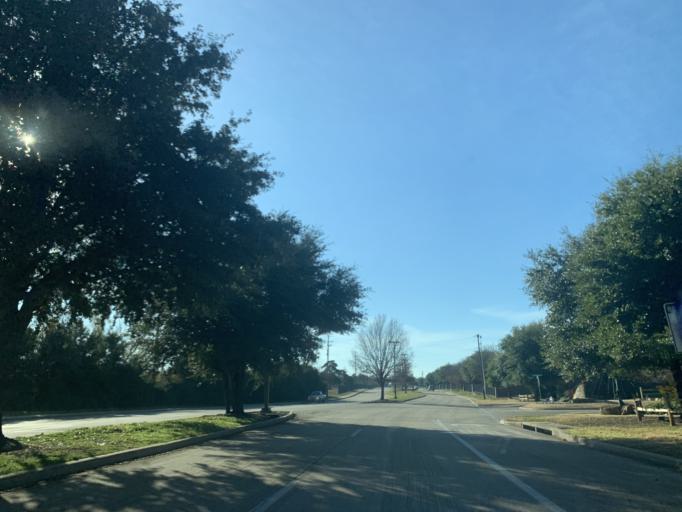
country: US
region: Texas
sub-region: Dallas County
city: DeSoto
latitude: 32.5808
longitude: -96.8399
